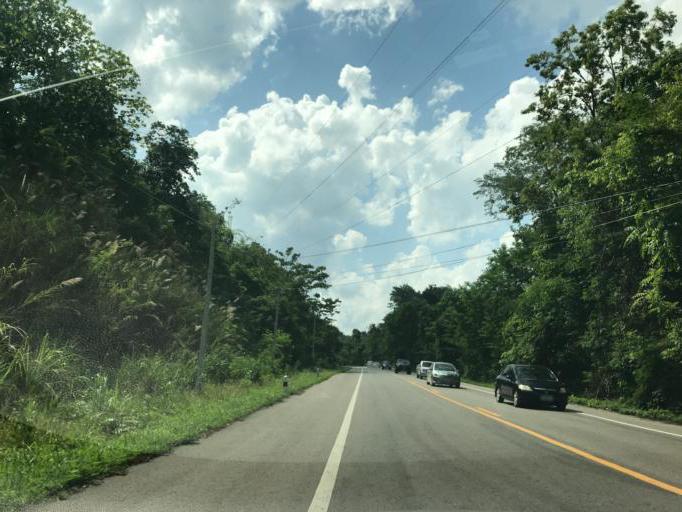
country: TH
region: Phayao
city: Phayao
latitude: 19.0858
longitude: 99.8163
